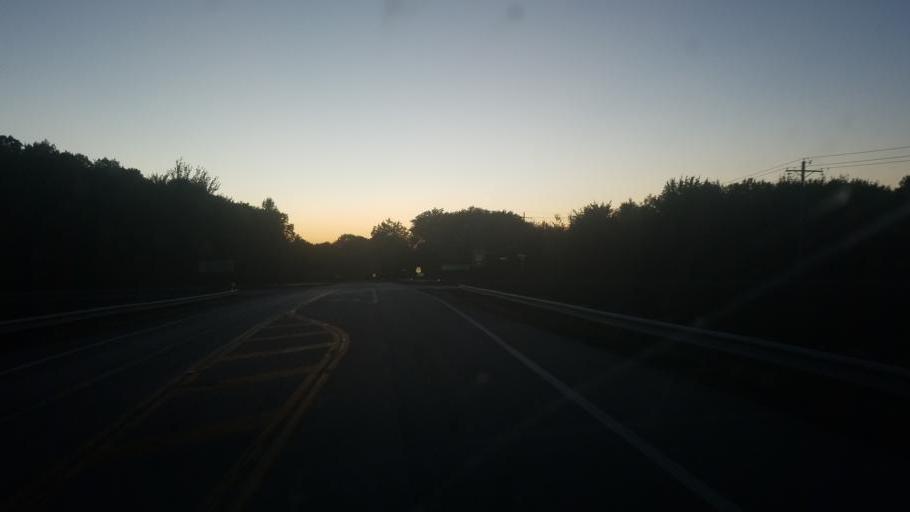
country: US
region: Ohio
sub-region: Ashtabula County
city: Jefferson
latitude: 41.7512
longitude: -80.7122
